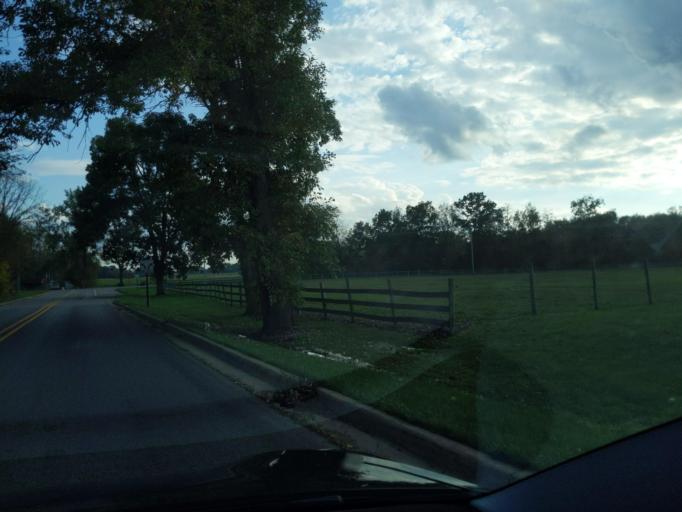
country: US
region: Michigan
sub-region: Jackson County
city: Jackson
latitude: 42.2880
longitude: -84.4626
